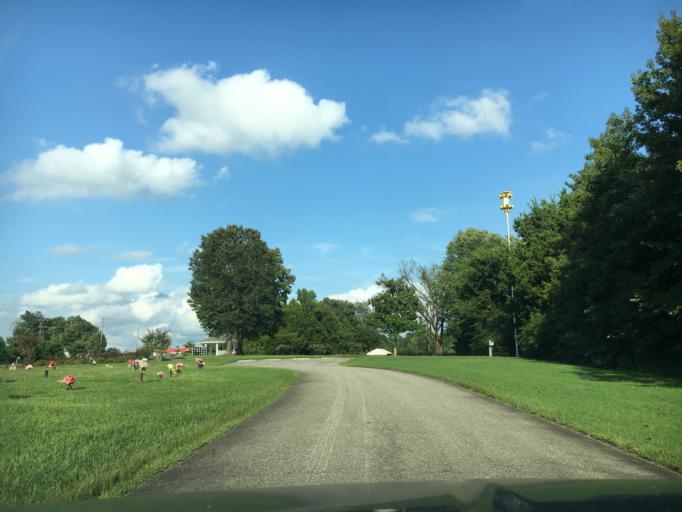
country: US
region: Virginia
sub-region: Halifax County
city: Halifax
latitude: 36.7325
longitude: -78.9152
